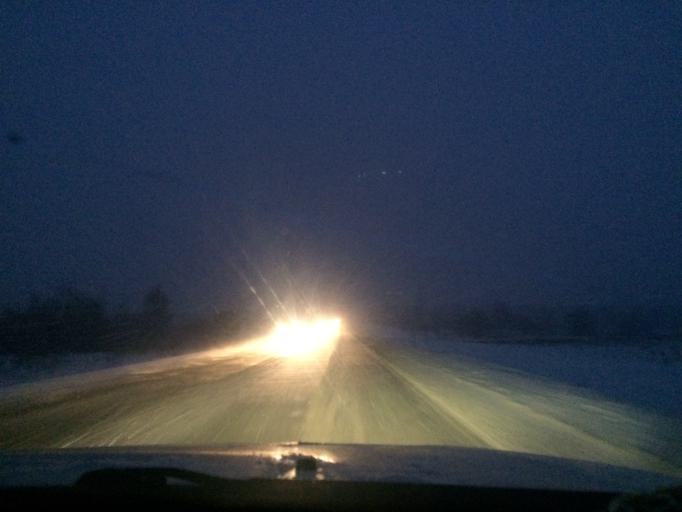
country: RU
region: Tula
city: Kosaya Gora
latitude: 54.1577
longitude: 37.5258
